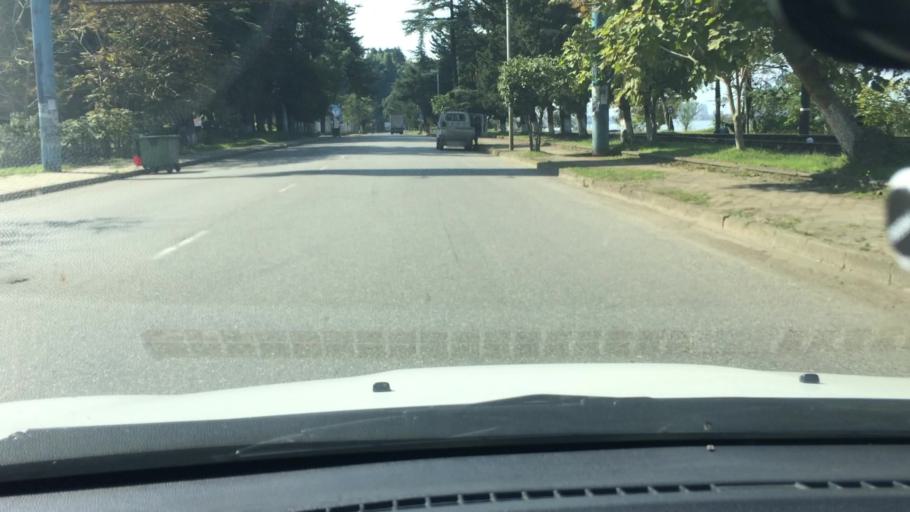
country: GE
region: Ajaria
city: Makhinjauri
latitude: 41.6752
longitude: 41.6948
